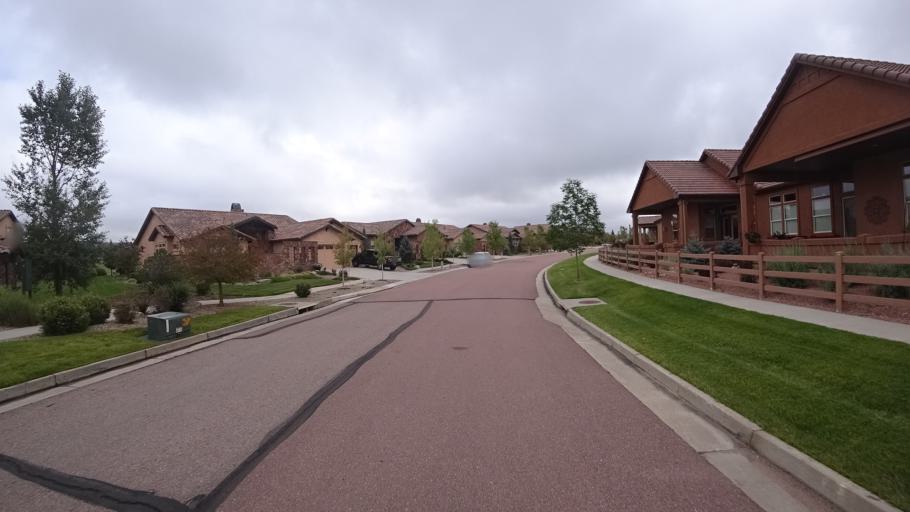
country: US
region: Colorado
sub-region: El Paso County
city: Gleneagle
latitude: 39.0217
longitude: -104.7842
